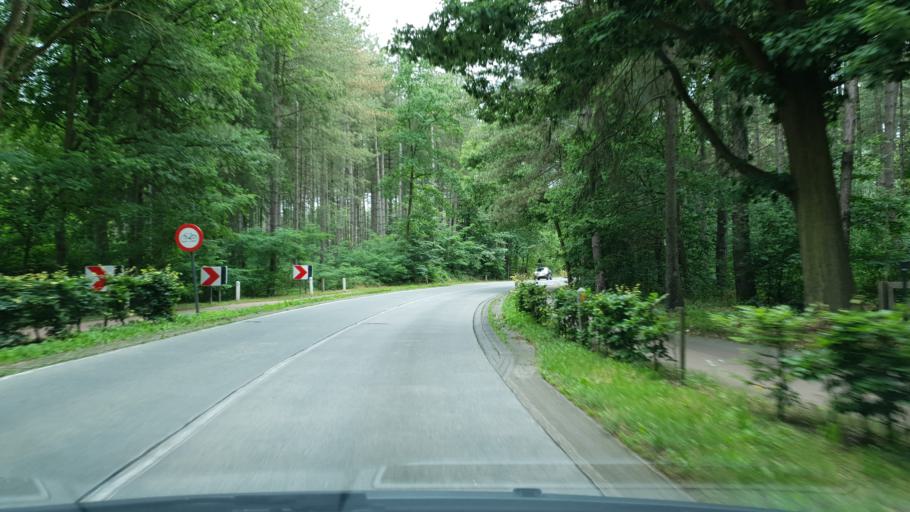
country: BE
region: Flanders
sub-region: Provincie Antwerpen
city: Westerlo
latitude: 51.0839
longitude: 4.8985
